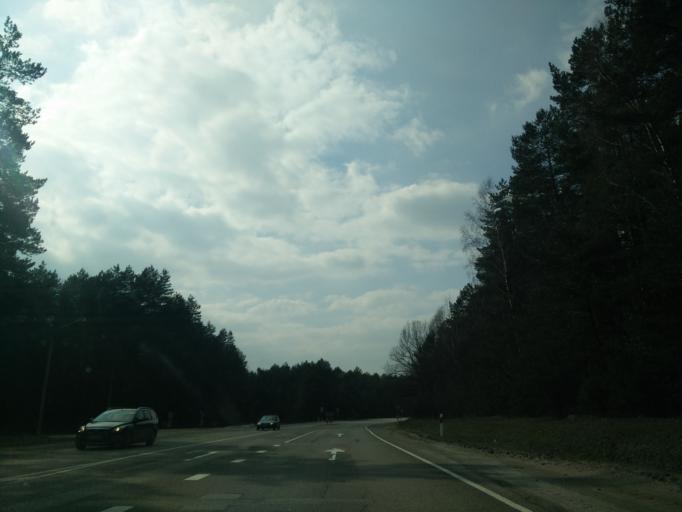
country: LT
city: Baltoji Voke
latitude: 54.6361
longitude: 25.1730
